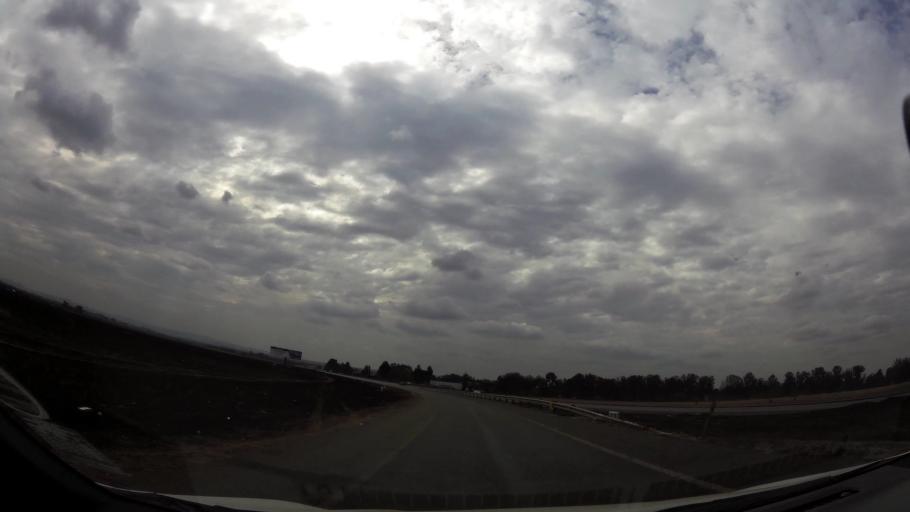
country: ZA
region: Gauteng
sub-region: Sedibeng District Municipality
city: Meyerton
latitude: -26.4142
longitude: 28.0772
